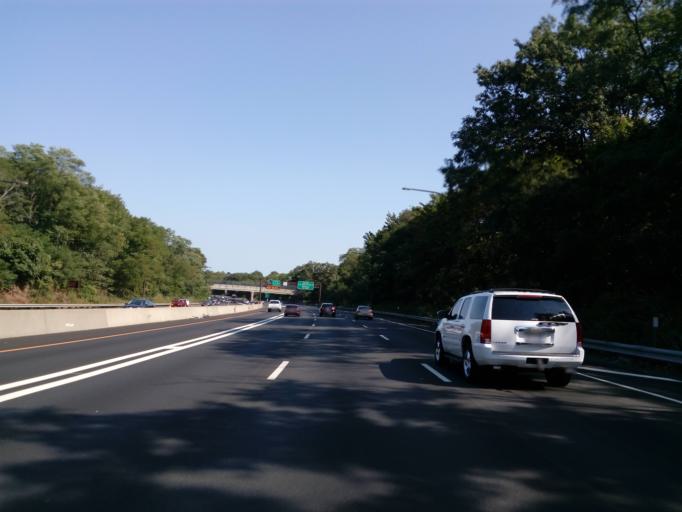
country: US
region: New York
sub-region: Nassau County
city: Old Westbury
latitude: 40.7798
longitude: -73.5800
